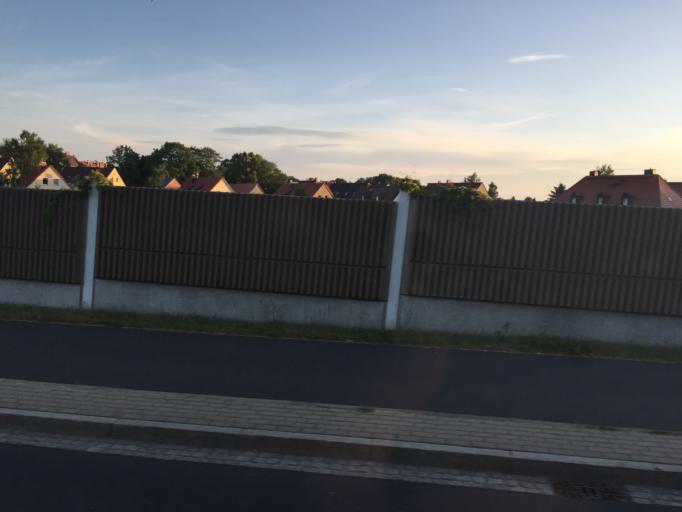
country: DE
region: Saxony
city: Goerlitz
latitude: 51.1511
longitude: 14.9522
